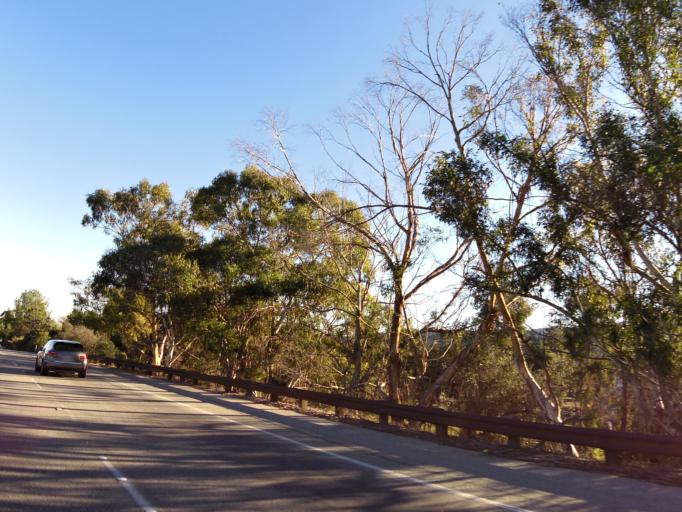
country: US
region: California
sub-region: Santa Clara County
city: Los Altos Hills
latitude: 37.3669
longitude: -122.1378
